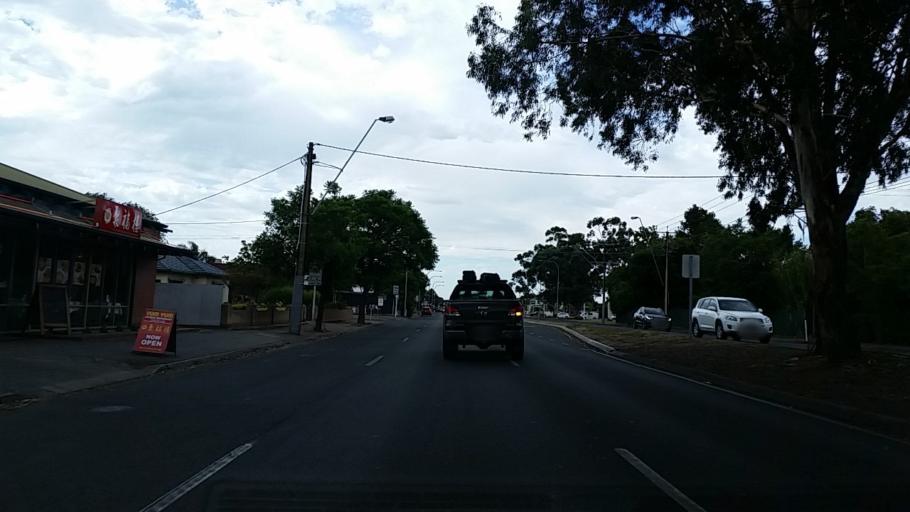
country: AU
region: South Australia
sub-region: Mitcham
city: Clarence Gardens
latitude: -34.9791
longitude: 138.5917
